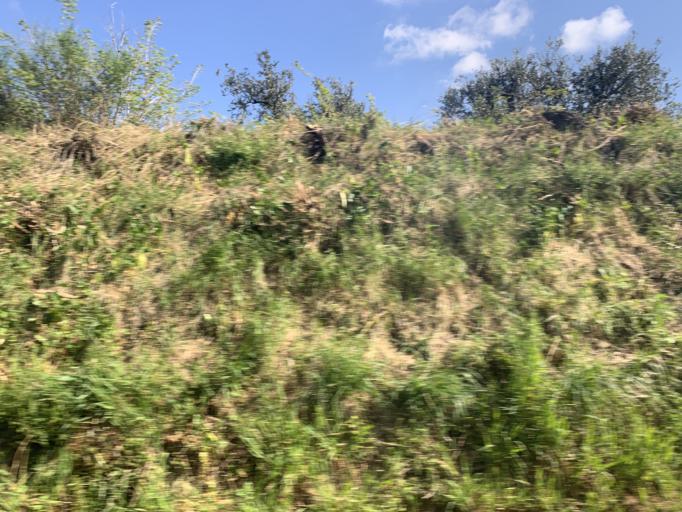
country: IT
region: Latium
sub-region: Citta metropolitana di Roma Capitale
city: Marino
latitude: 41.7849
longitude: 12.6483
